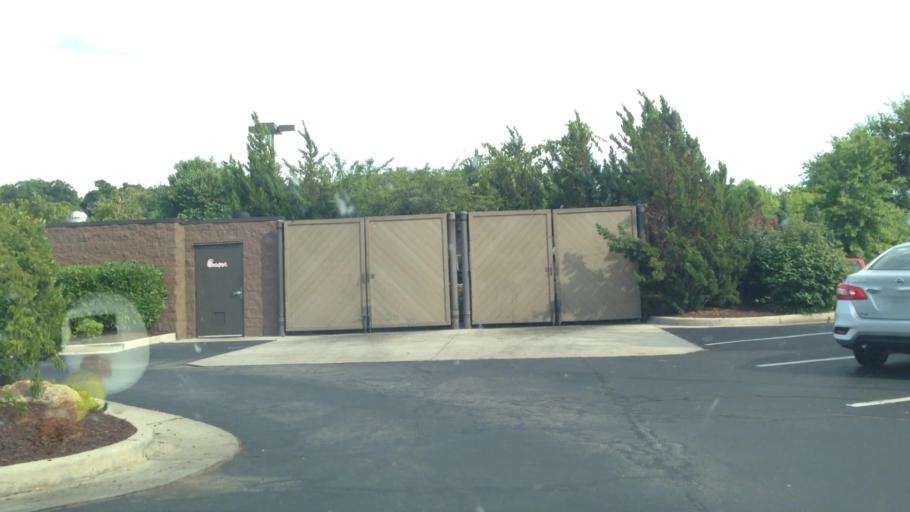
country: US
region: Virginia
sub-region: City of Danville
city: Danville
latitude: 36.5818
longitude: -79.4289
